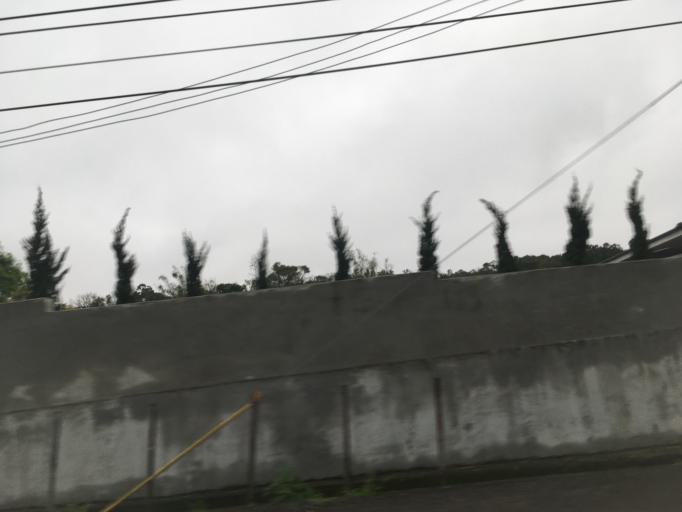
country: TW
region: Taiwan
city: Fengyuan
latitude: 24.4193
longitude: 120.7320
